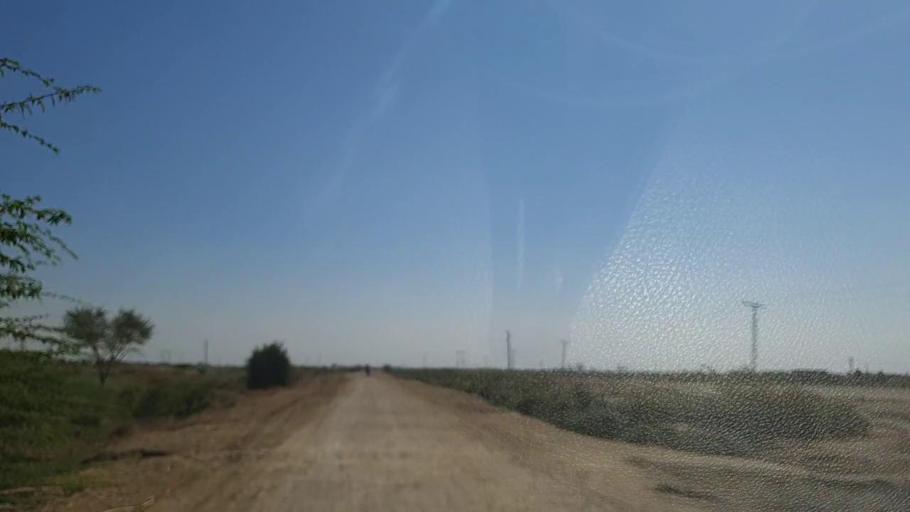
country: PK
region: Sindh
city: Samaro
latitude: 25.3074
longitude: 69.4782
